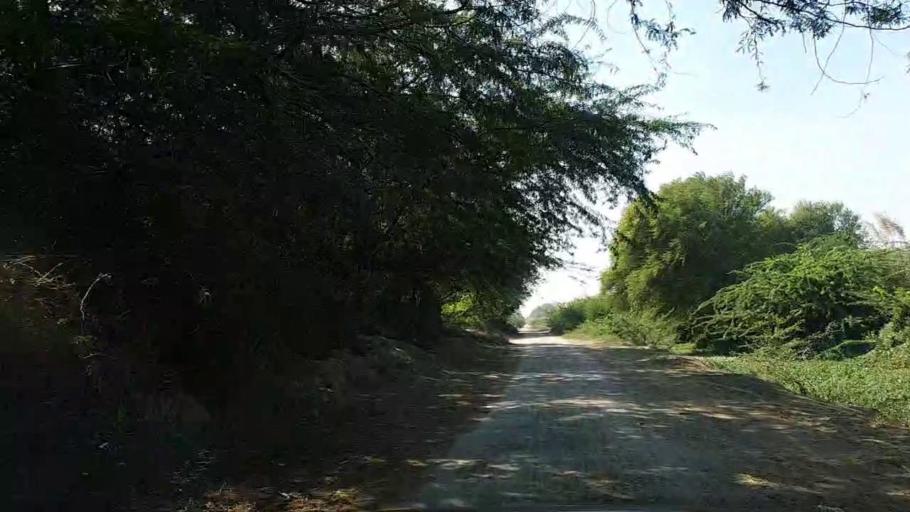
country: PK
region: Sindh
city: Daro Mehar
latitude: 24.8374
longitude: 68.1049
